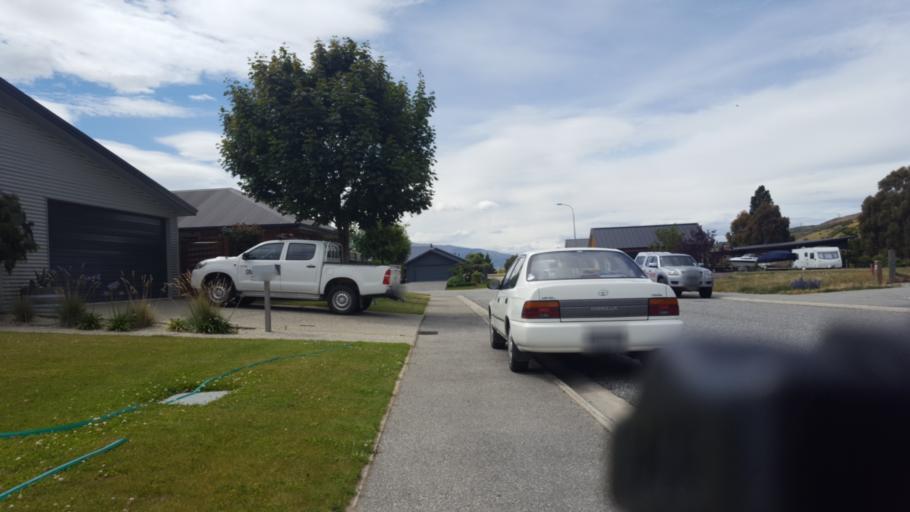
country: NZ
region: Otago
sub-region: Queenstown-Lakes District
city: Wanaka
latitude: -45.0397
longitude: 169.2179
